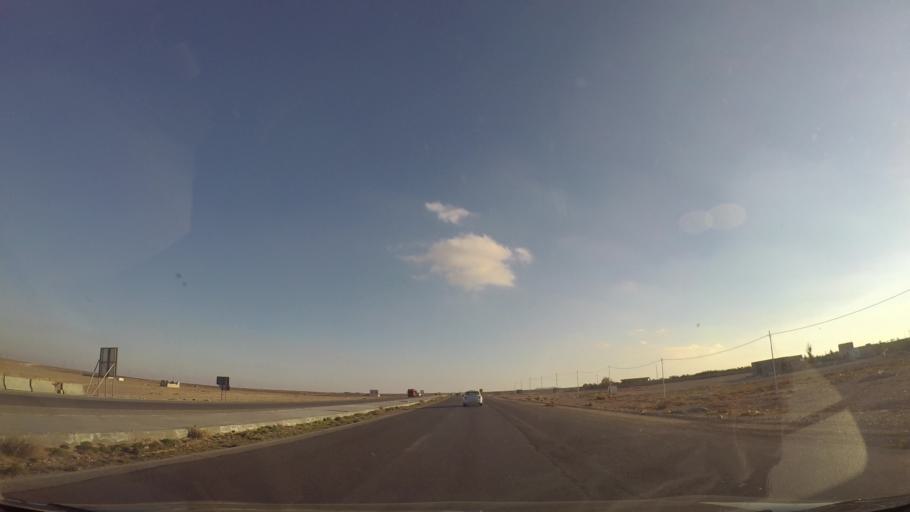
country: JO
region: Tafielah
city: Busayra
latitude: 30.5727
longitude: 35.7985
